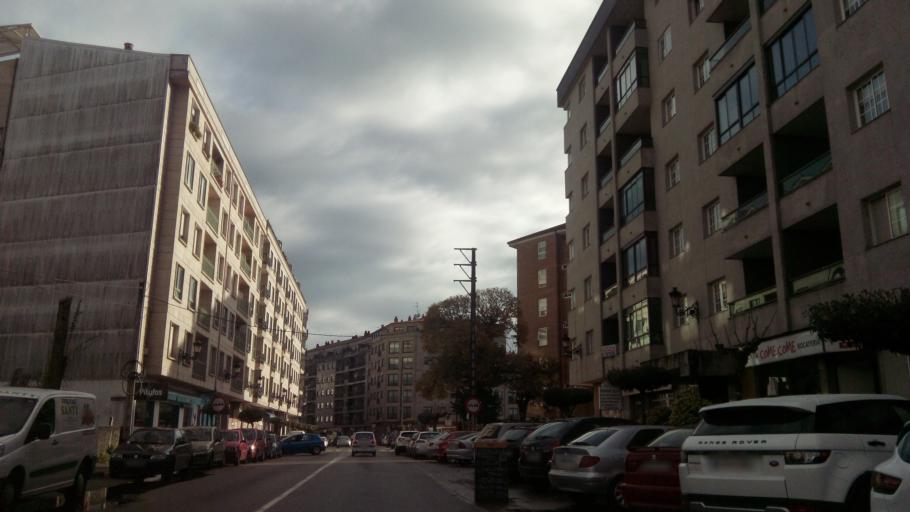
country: ES
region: Galicia
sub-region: Provincia de Pontevedra
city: Ponteareas
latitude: 42.1723
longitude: -8.5084
